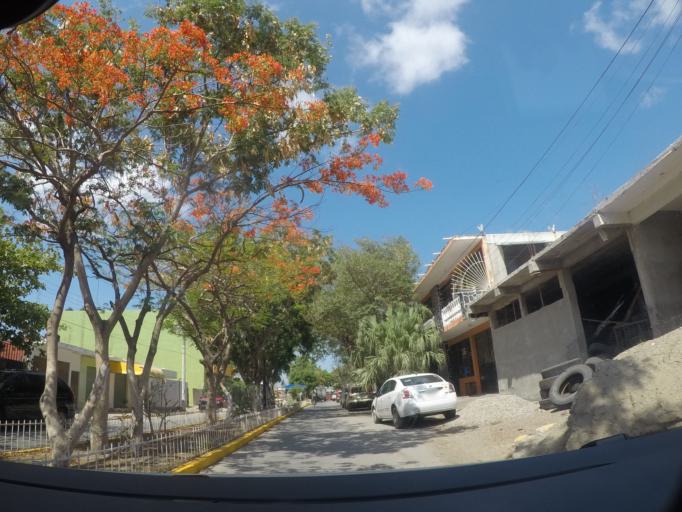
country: MX
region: Oaxaca
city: Juchitan de Zaragoza
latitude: 16.4362
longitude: -95.0159
